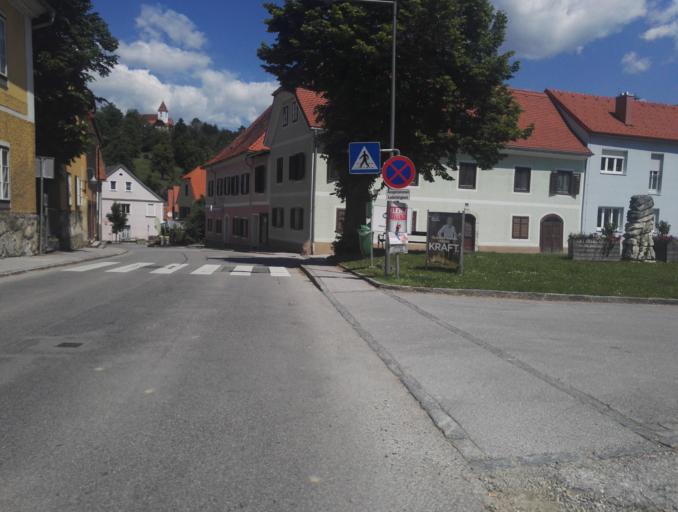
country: AT
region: Styria
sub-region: Politischer Bezirk Graz-Umgebung
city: Peggau
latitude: 47.1978
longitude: 15.3363
